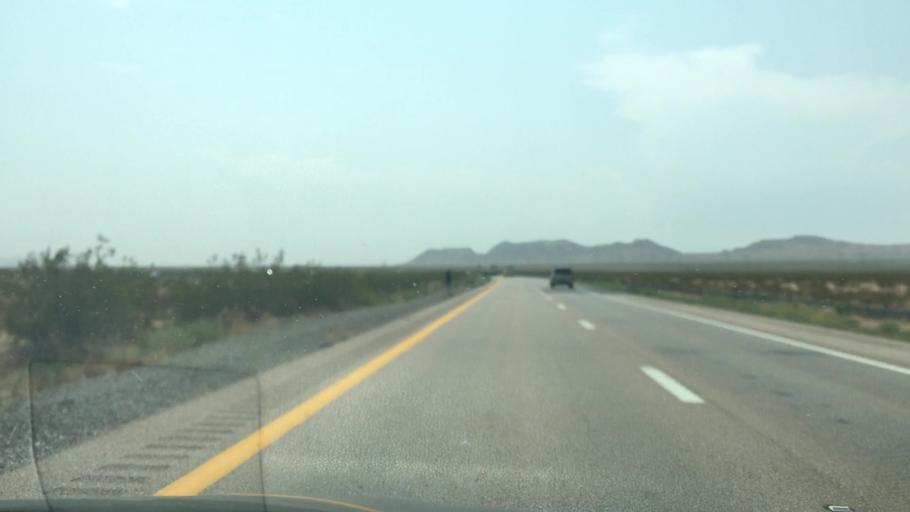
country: US
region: Nevada
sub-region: Clark County
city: Moapa Valley
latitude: 36.7470
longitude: -114.4145
